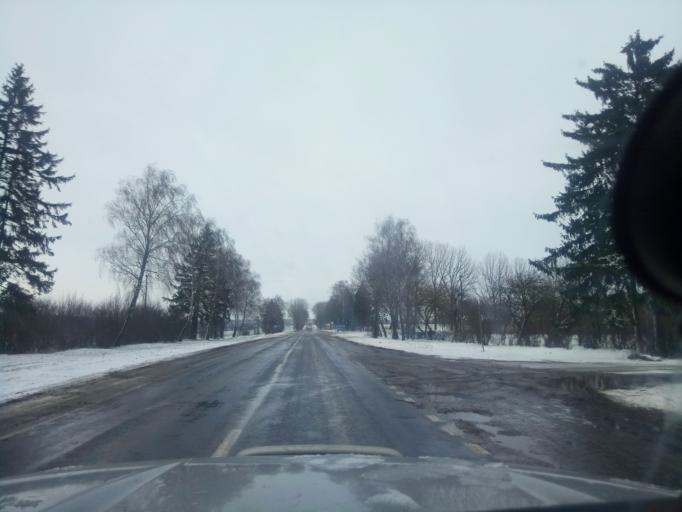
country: BY
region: Minsk
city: Tsimkavichy
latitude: 53.0896
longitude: 27.0259
